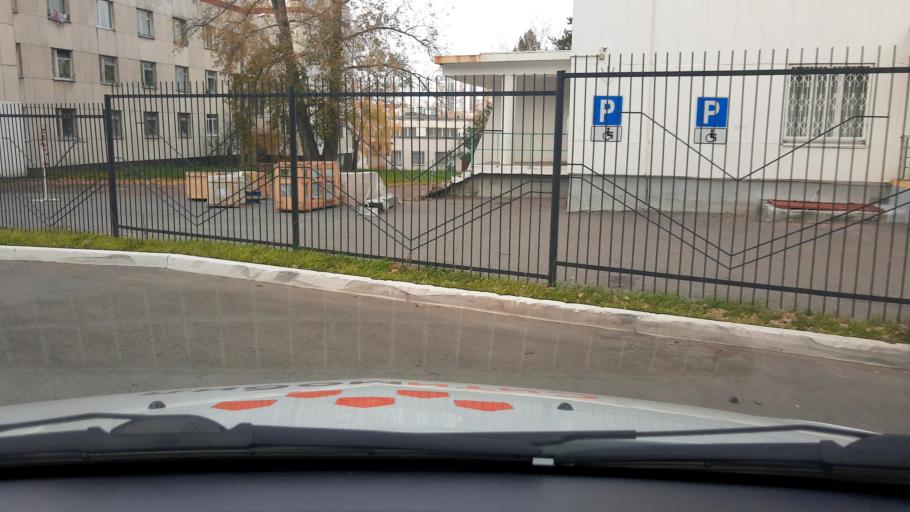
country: RU
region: Bashkortostan
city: Ufa
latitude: 54.7380
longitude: 56.0173
